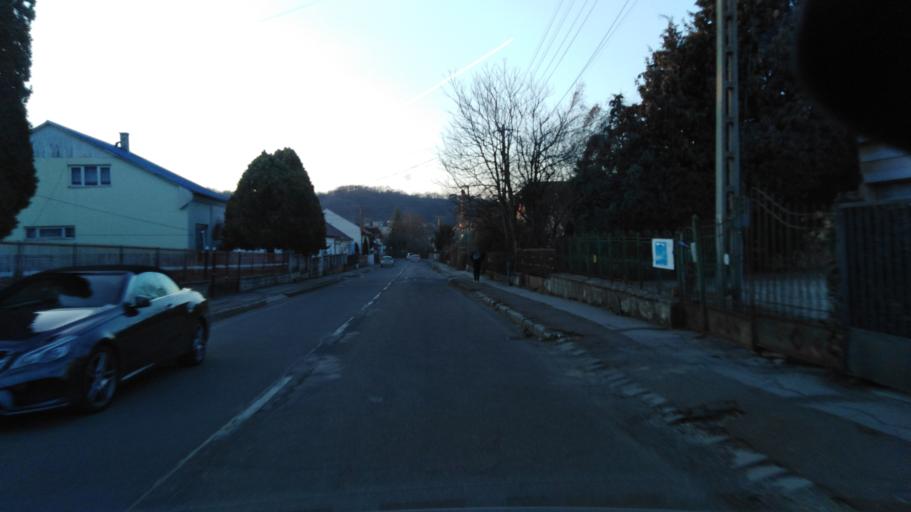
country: HU
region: Nograd
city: Salgotarjan
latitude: 48.0939
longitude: 19.8052
